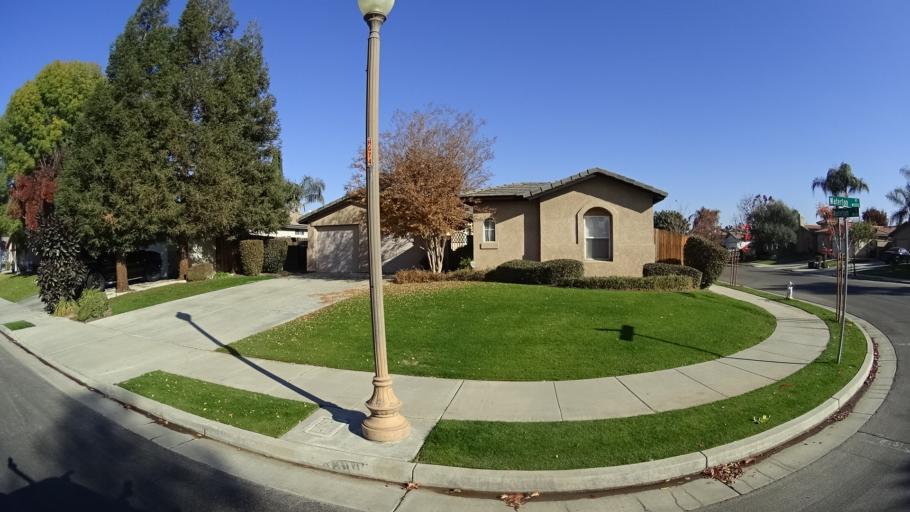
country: US
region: California
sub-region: Kern County
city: Rosedale
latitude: 35.3259
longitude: -119.1321
